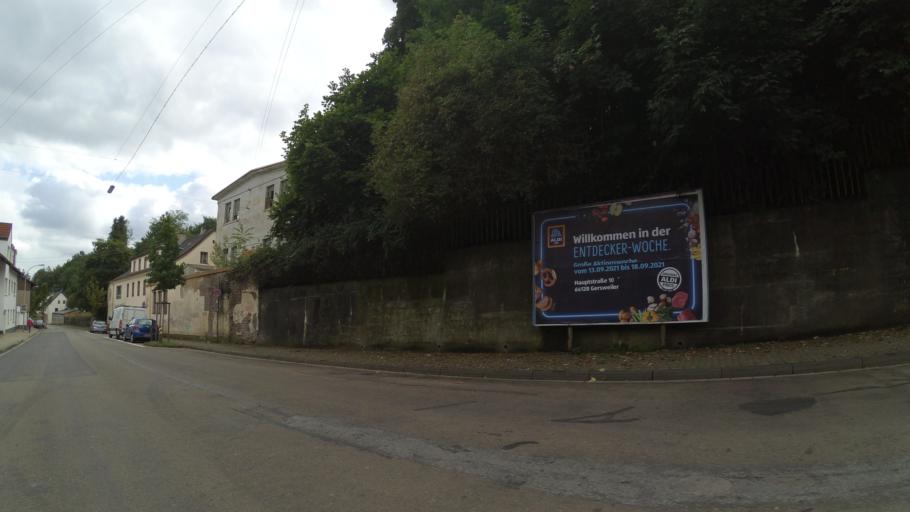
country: FR
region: Lorraine
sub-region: Departement de la Moselle
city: Schoeneck
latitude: 49.2368
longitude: 6.9383
